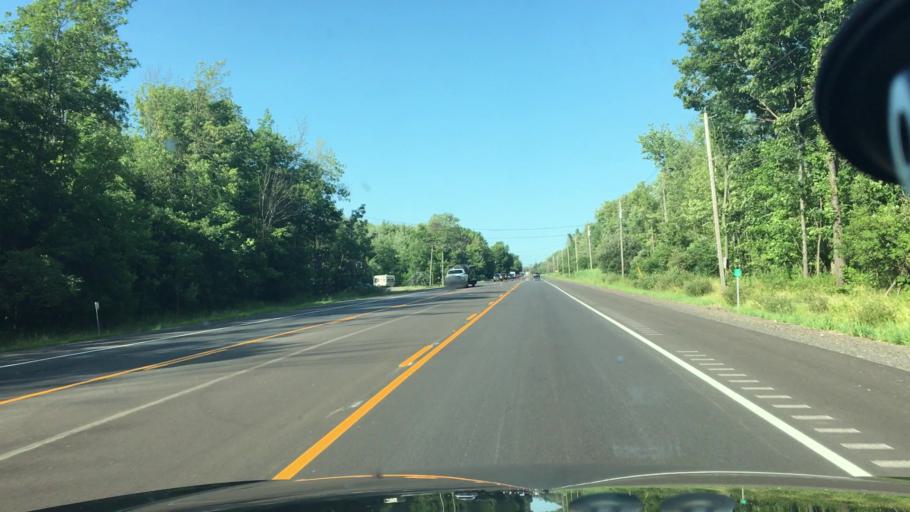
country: US
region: New York
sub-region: Erie County
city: Wanakah
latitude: 42.7184
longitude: -78.9030
